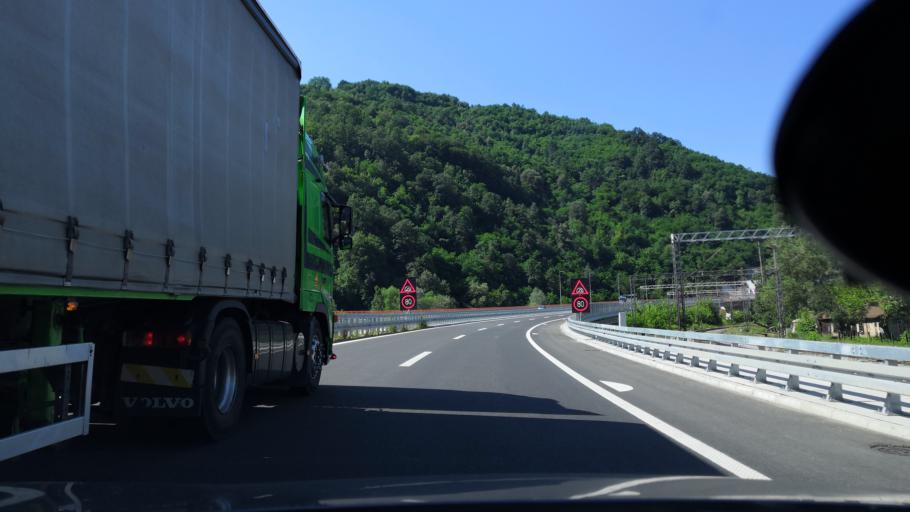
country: RS
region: Central Serbia
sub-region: Jablanicki Okrug
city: Vlasotince
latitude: 42.8304
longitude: 22.1281
